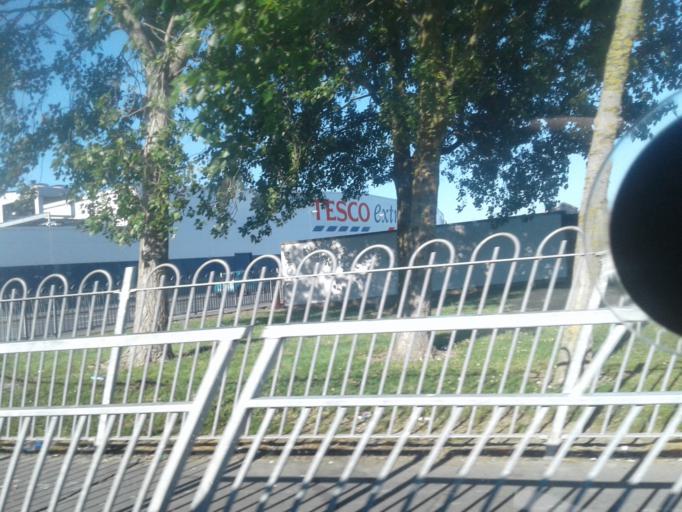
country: IE
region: Leinster
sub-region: Dublin City
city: Finglas
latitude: 53.3820
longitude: -6.2980
